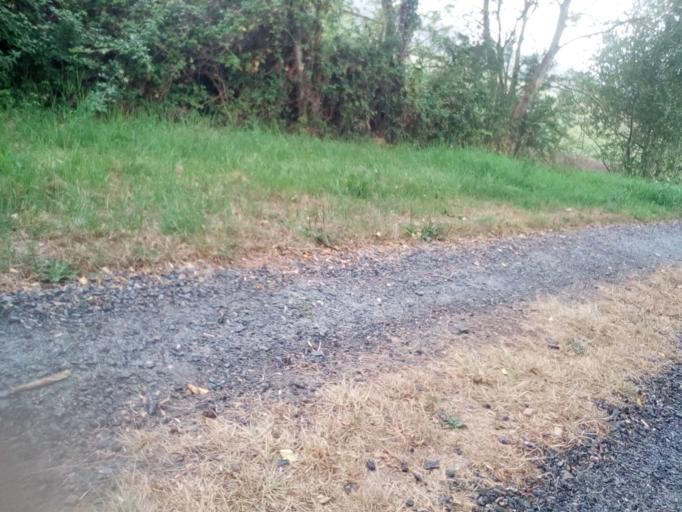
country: FR
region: Lower Normandy
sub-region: Departement du Calvados
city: Bavent
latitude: 49.2361
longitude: -0.1537
